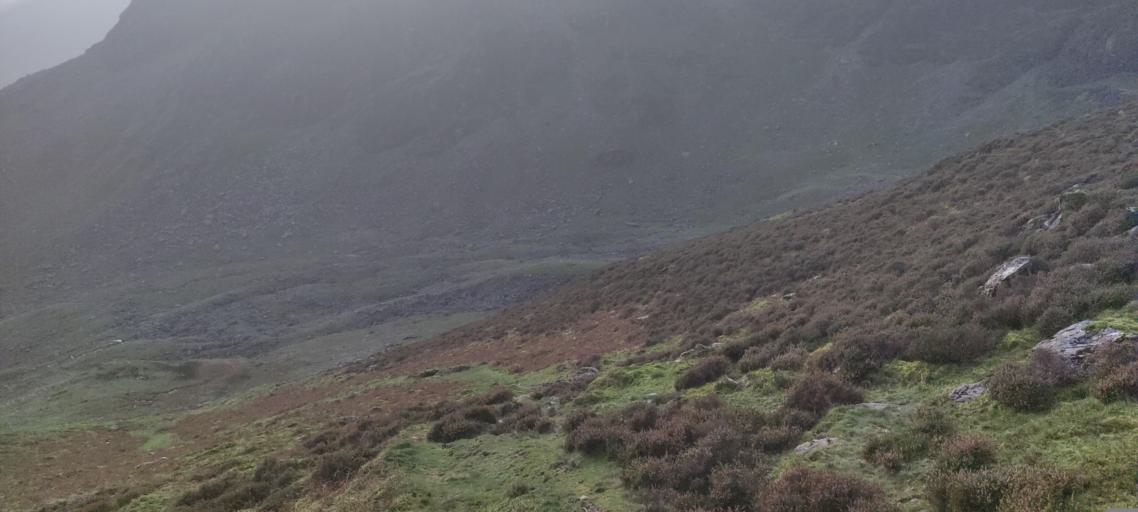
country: GB
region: England
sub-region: Cumbria
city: Keswick
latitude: 54.5241
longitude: -3.2726
